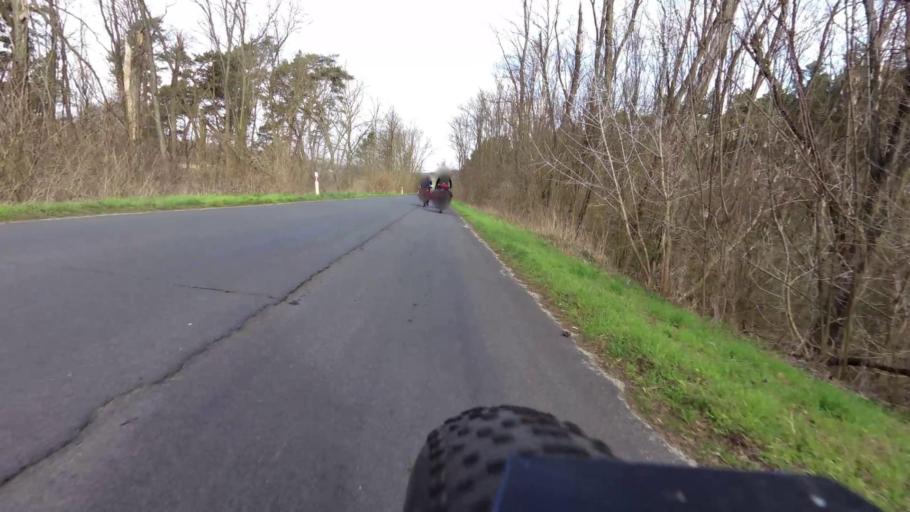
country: DE
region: Brandenburg
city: Brieskow-Finkenheerd
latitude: 52.2959
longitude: 14.6033
